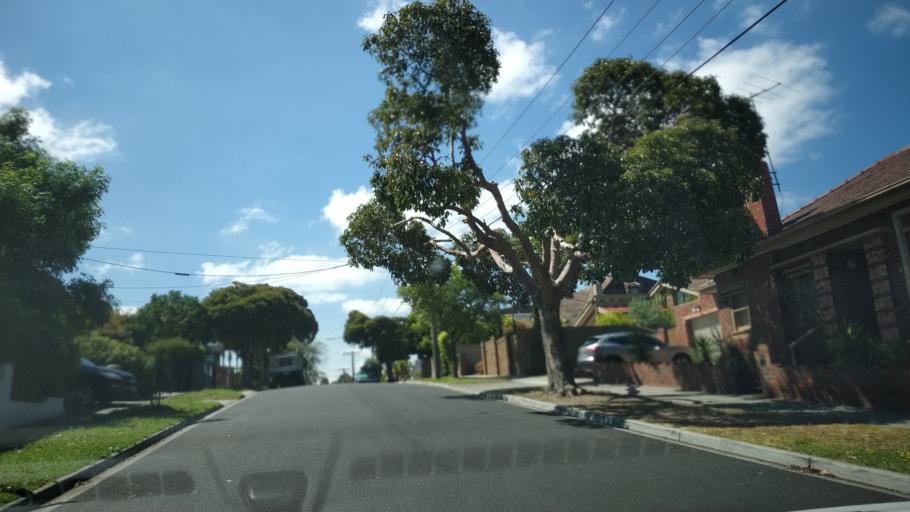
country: AU
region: Victoria
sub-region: Glen Eira
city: Caulfield South
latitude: -37.8947
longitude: 145.0277
